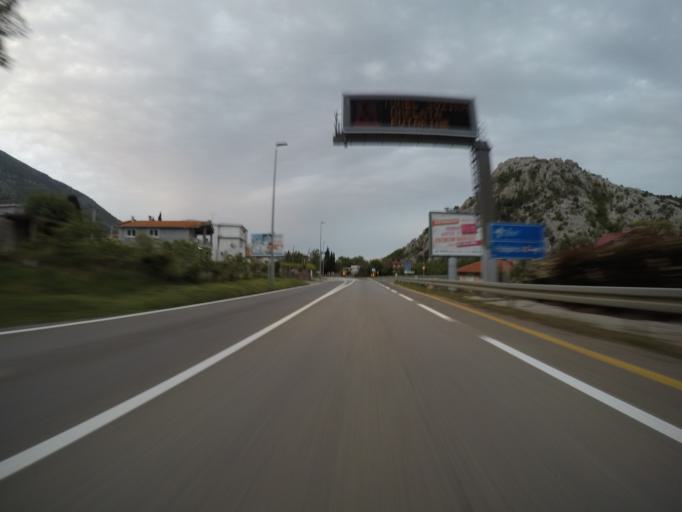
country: ME
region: Bar
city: Sutomore
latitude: 42.1545
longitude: 19.0323
